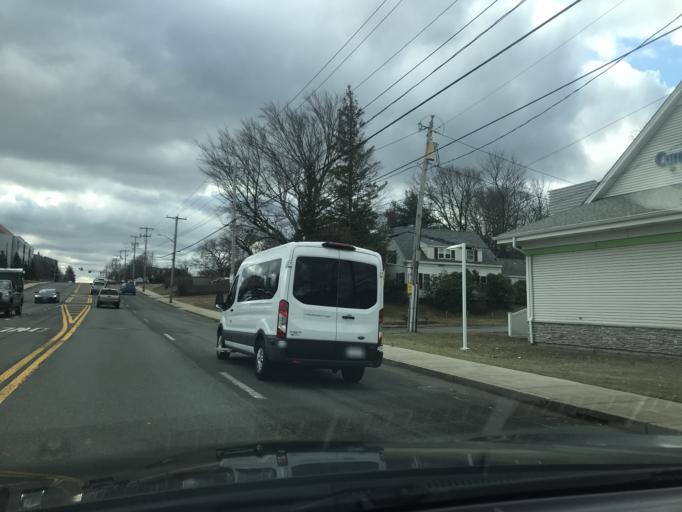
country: US
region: Massachusetts
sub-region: Norfolk County
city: Weymouth
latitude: 42.1794
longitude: -70.9554
